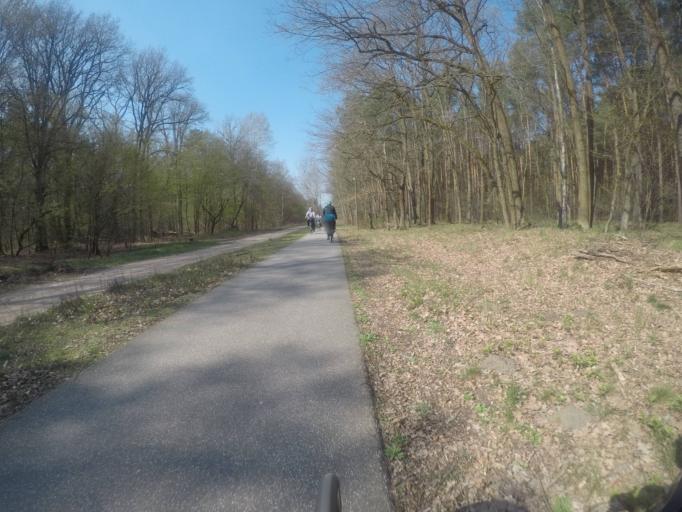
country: DE
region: Brandenburg
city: Hennigsdorf
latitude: 52.6401
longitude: 13.1784
